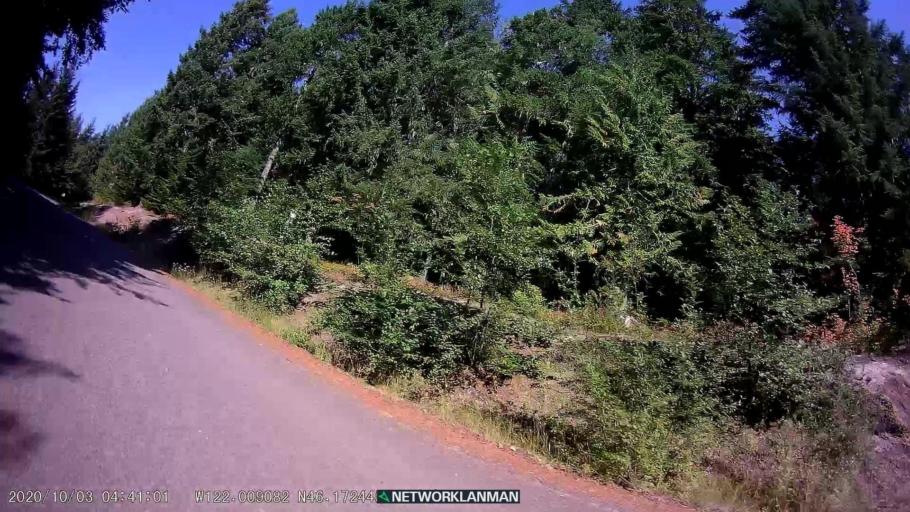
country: US
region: Washington
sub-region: Lewis County
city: Morton
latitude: 46.1727
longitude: -122.0092
